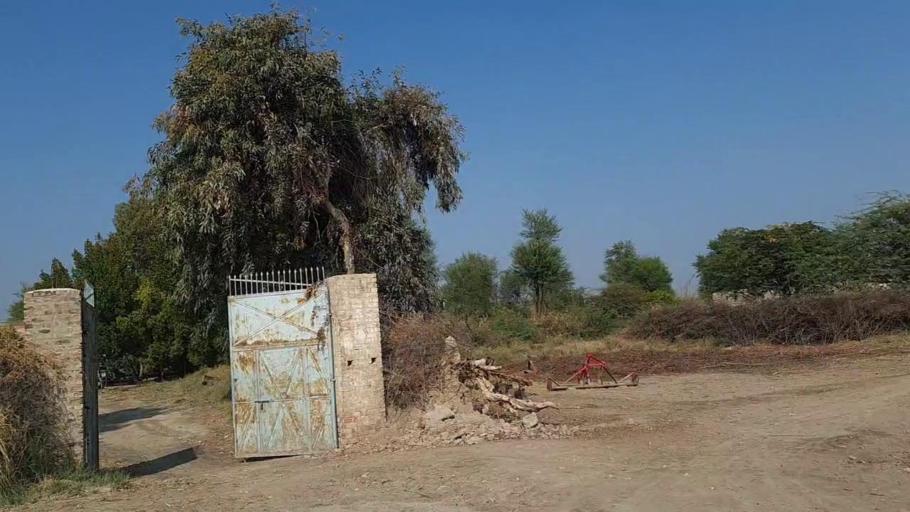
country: PK
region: Sindh
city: Jam Sahib
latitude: 26.2553
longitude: 68.5838
